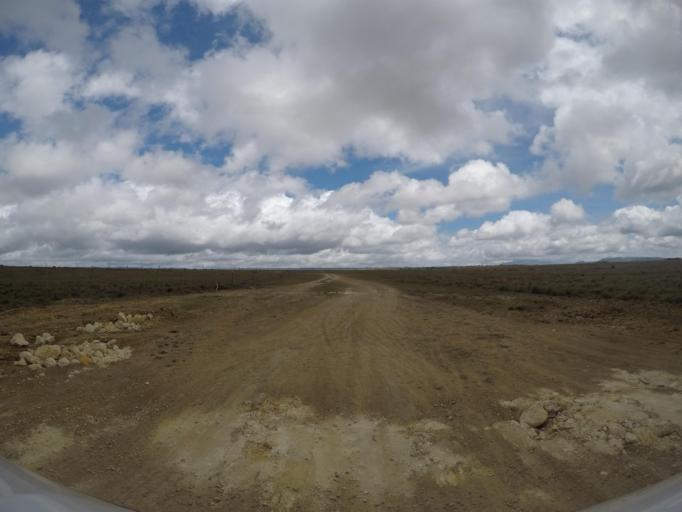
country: TL
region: Lautem
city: Lospalos
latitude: -8.4500
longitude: 126.9860
